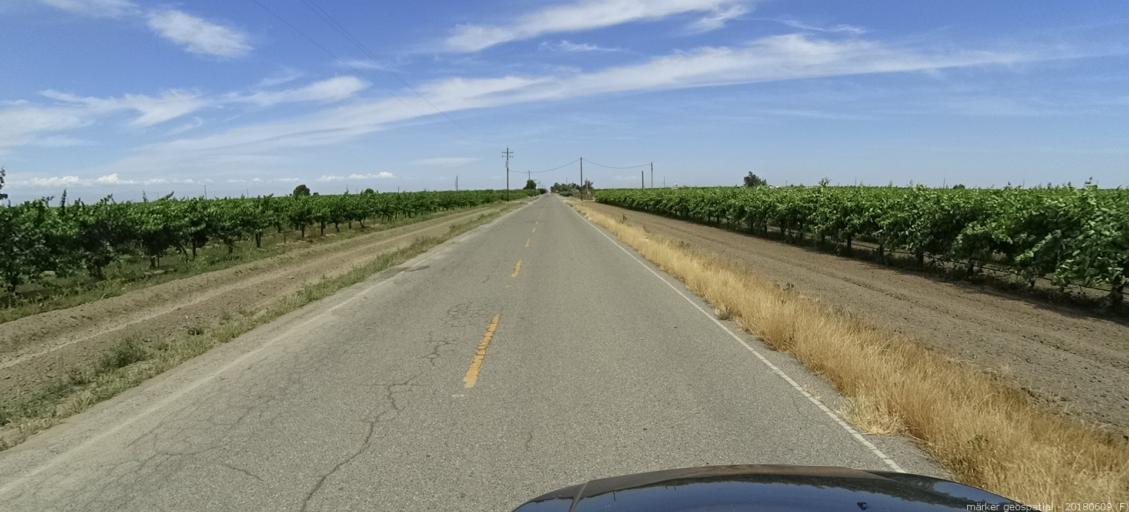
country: US
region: California
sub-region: Madera County
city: Parkwood
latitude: 36.9092
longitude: -120.1165
